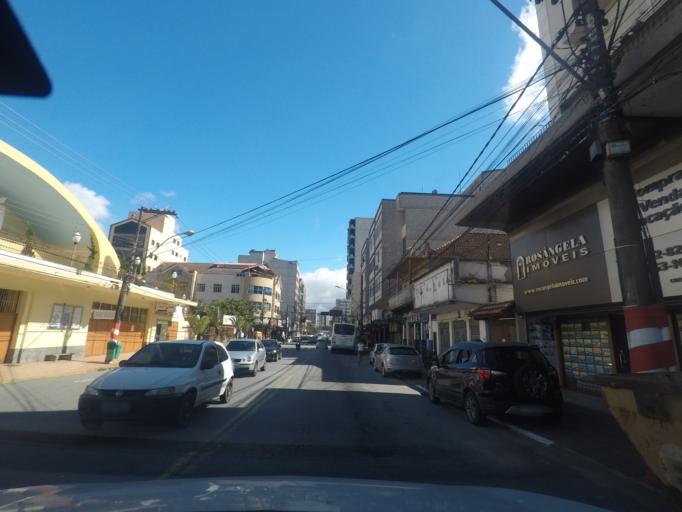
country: BR
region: Rio de Janeiro
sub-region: Teresopolis
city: Teresopolis
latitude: -22.4407
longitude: -42.9801
